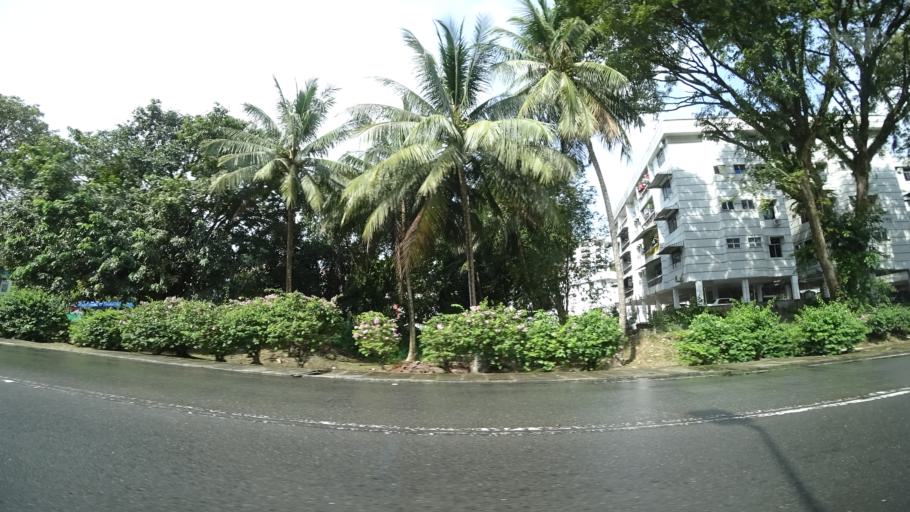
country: BN
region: Brunei and Muara
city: Bandar Seri Begawan
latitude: 4.8869
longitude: 114.9305
